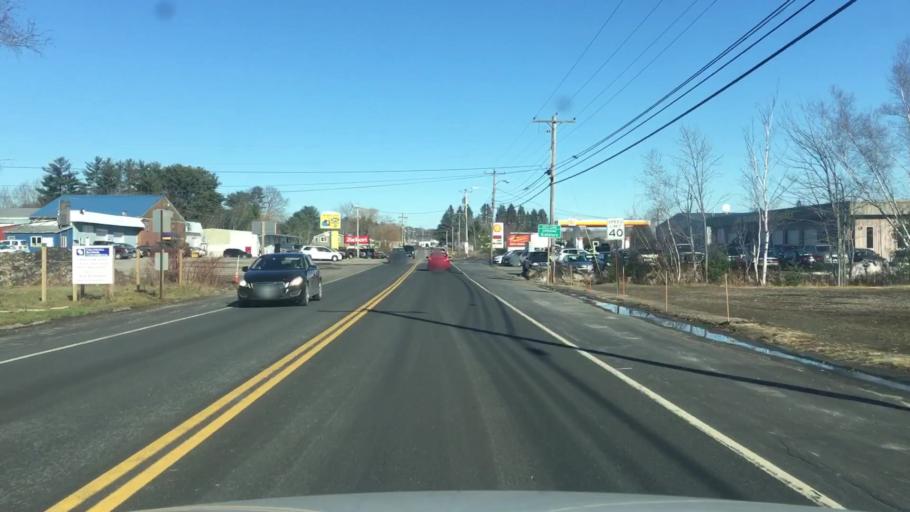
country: US
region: Maine
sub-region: York County
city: Biddeford
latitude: 43.4594
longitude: -70.4923
